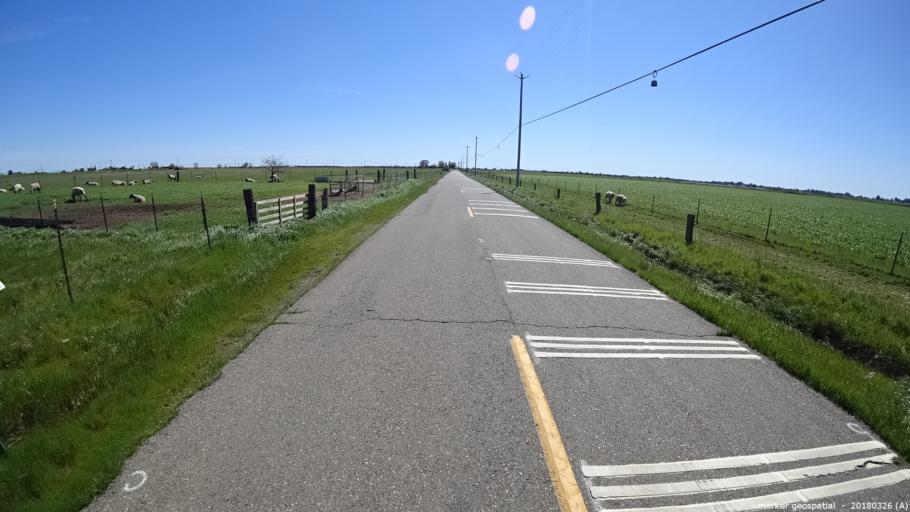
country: US
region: California
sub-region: Sacramento County
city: Wilton
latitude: 38.4752
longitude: -121.2608
